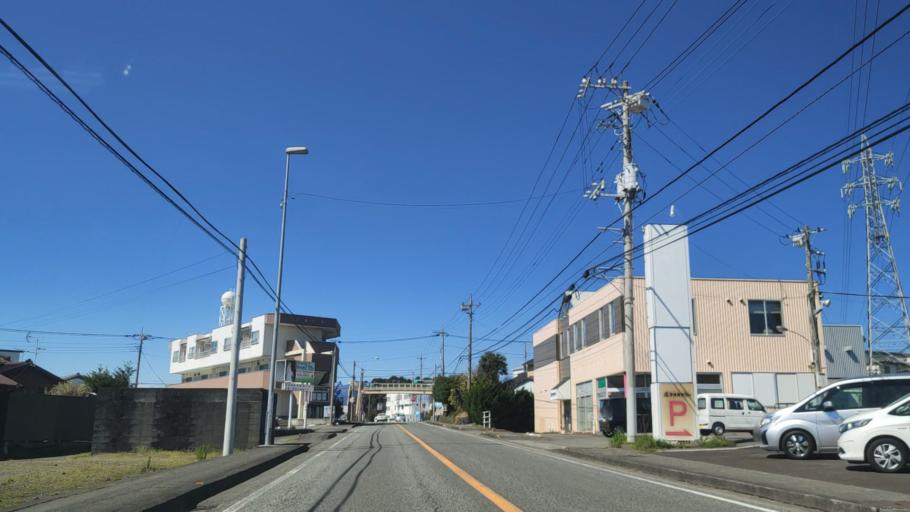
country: JP
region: Shizuoka
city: Fujinomiya
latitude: 35.2048
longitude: 138.6412
